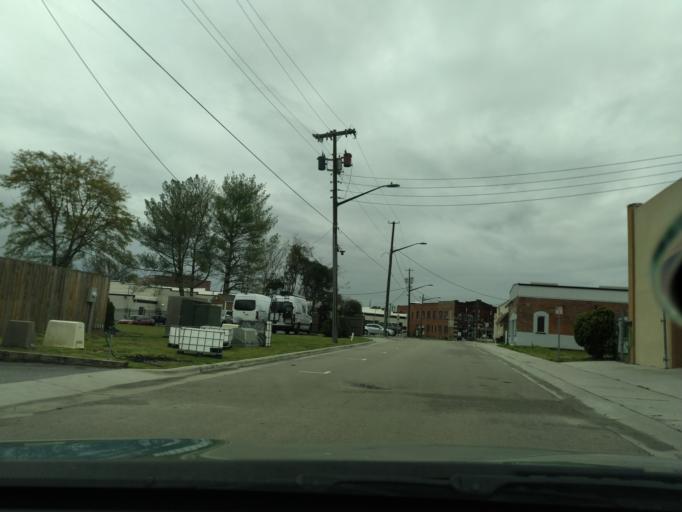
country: US
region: North Carolina
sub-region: Pitt County
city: Greenville
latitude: 35.6096
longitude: -77.3780
